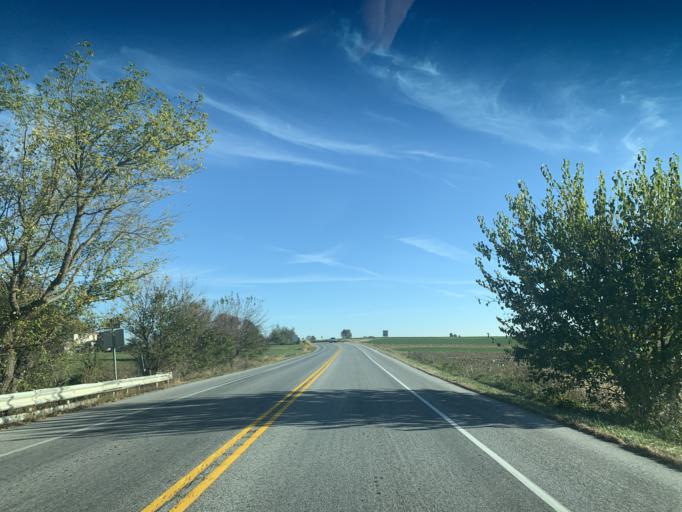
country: US
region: Pennsylvania
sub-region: Chester County
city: Oxford
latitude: 39.8435
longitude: -75.9383
